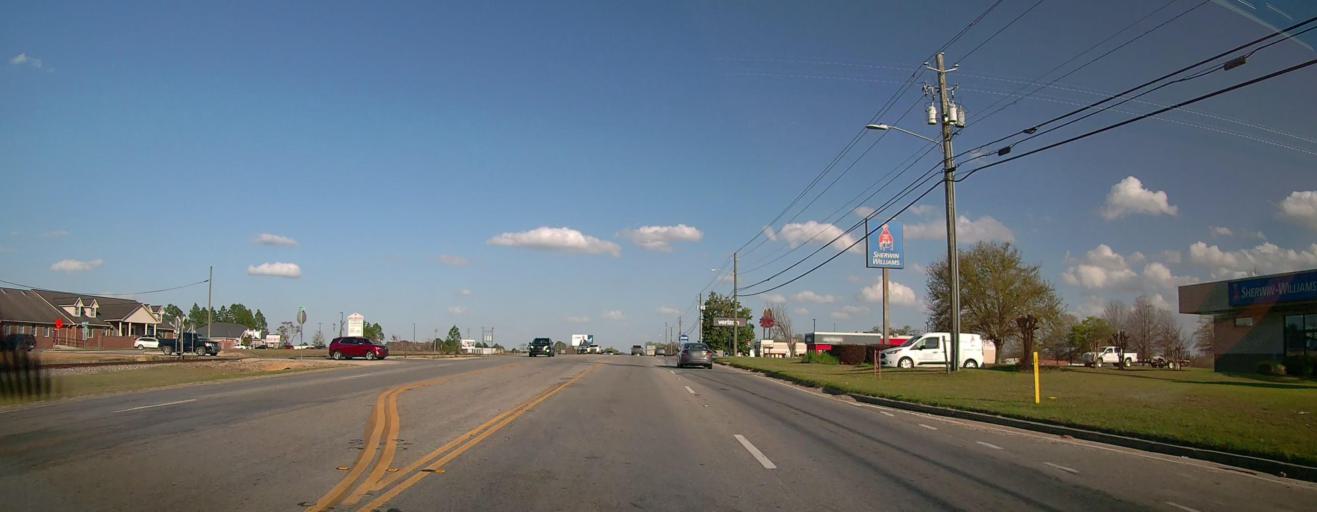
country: US
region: Georgia
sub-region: Toombs County
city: Lyons
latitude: 32.2049
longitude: -82.3623
